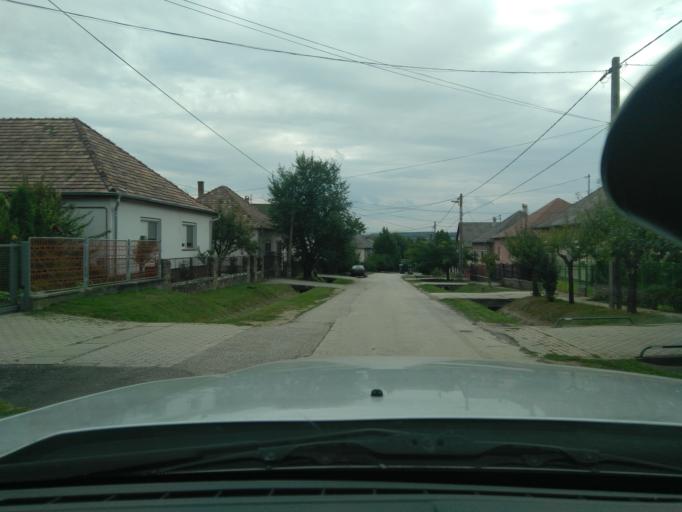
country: HU
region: Fejer
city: Val
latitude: 47.3710
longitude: 18.6820
